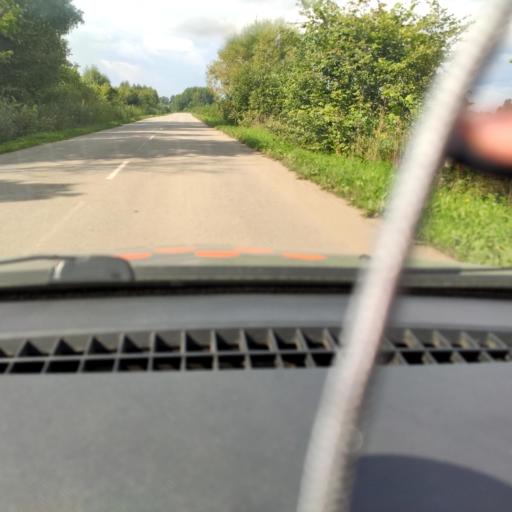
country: RU
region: Bashkortostan
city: Kudeyevskiy
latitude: 54.7363
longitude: 56.6053
